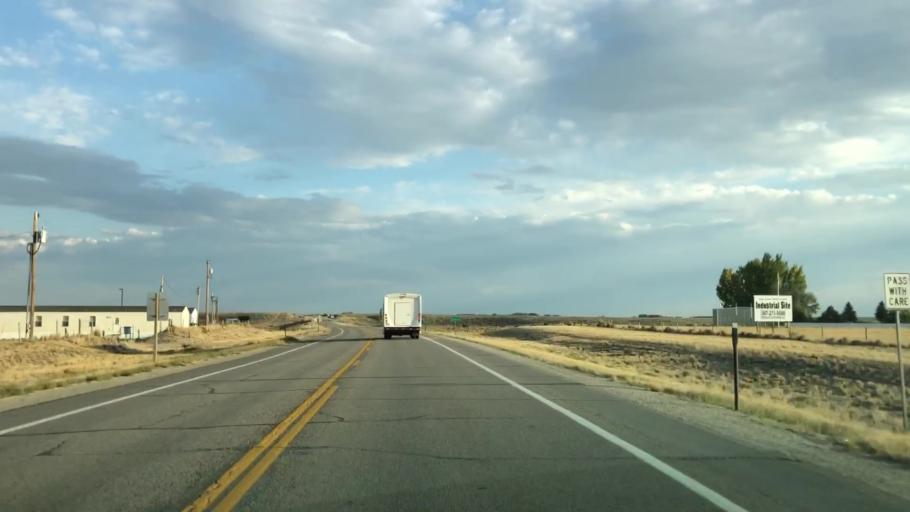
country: US
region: Wyoming
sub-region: Sweetwater County
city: North Rock Springs
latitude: 42.1055
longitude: -109.4481
